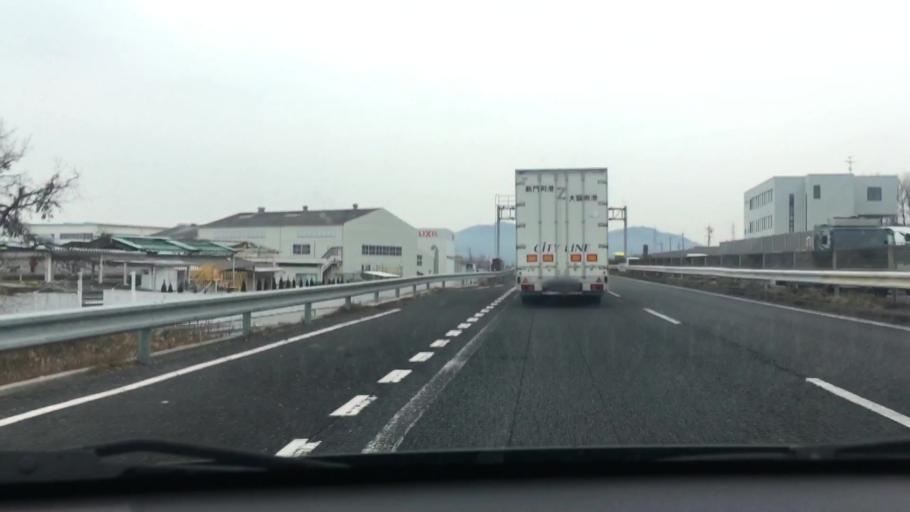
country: JP
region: Mie
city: Ueno-ebisumachi
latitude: 34.7584
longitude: 136.1511
